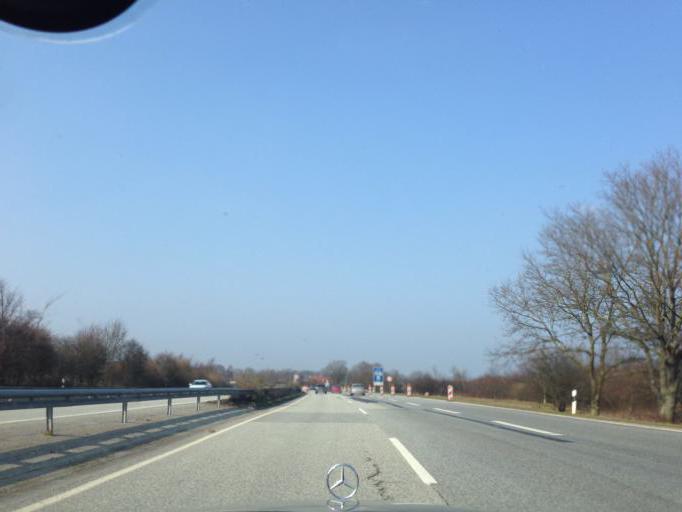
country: DE
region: Schleswig-Holstein
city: Schackendorf
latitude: 53.9486
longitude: 10.2757
